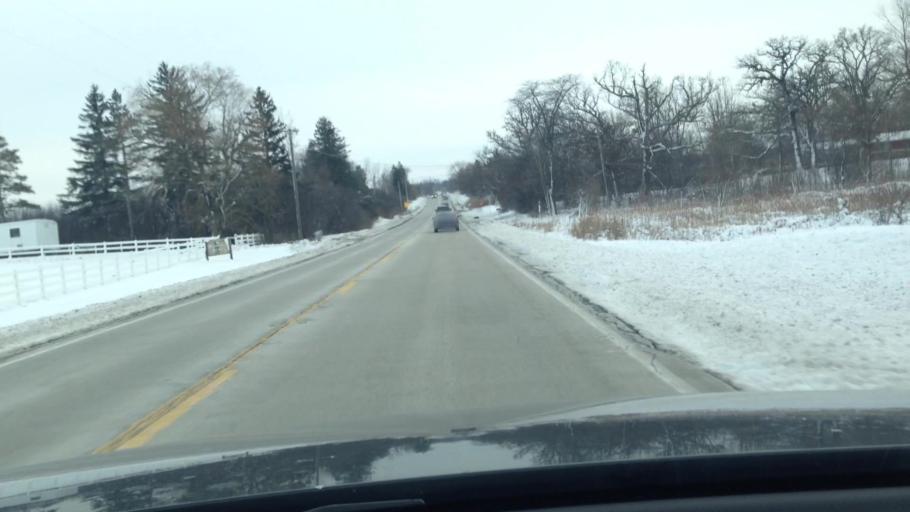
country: US
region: Illinois
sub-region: McHenry County
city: Woodstock
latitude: 42.2630
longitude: -88.4331
